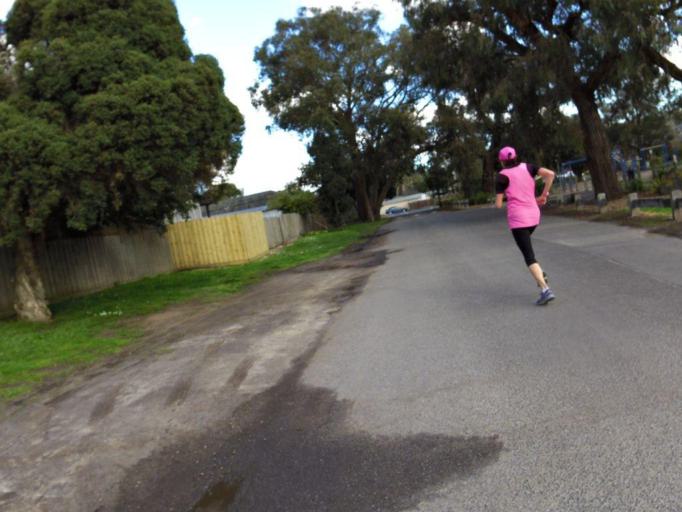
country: AU
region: Victoria
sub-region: Maroondah
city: Croydon South
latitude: -37.8114
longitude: 145.2794
